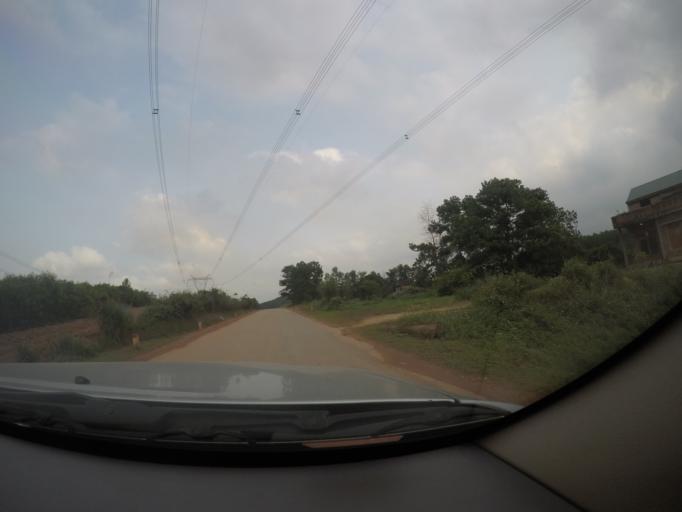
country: VN
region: Quang Binh
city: Kien Giang
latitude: 17.1194
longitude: 106.7965
